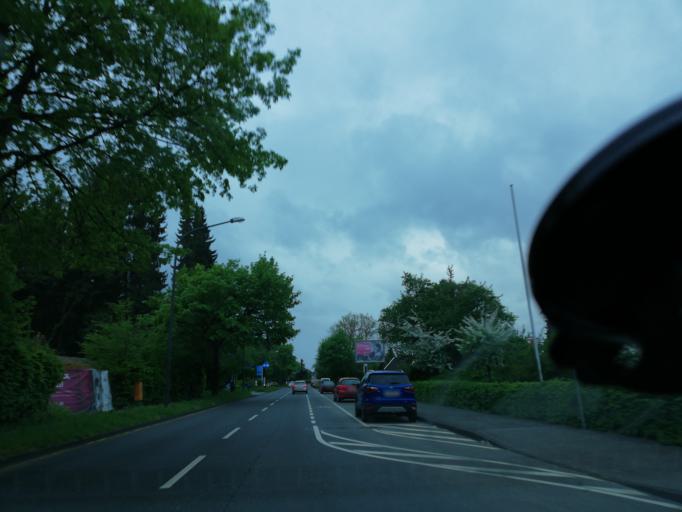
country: DE
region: North Rhine-Westphalia
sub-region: Regierungsbezirk Dusseldorf
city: Solingen
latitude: 51.2306
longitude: 7.0751
